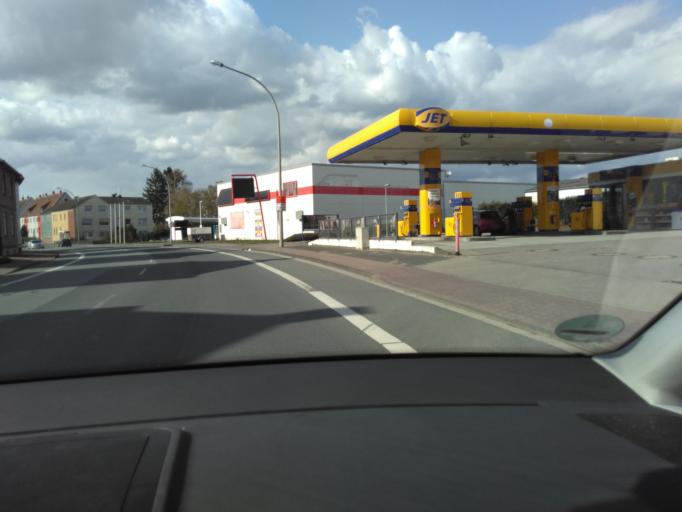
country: DE
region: North Rhine-Westphalia
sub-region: Regierungsbezirk Munster
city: Beckum
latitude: 51.7694
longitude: 8.0406
